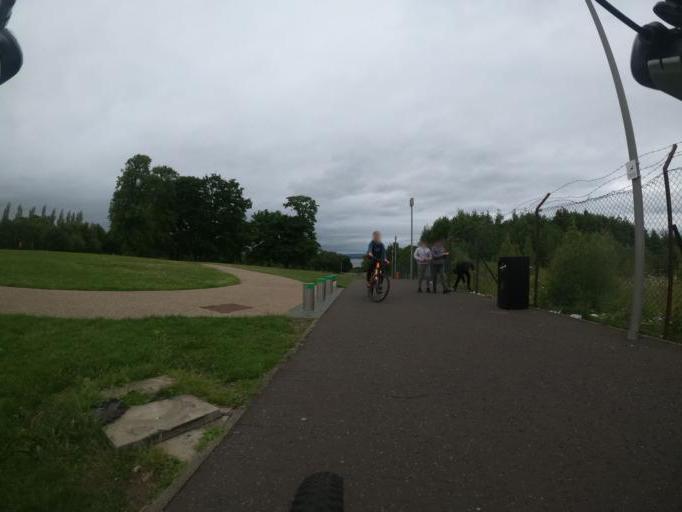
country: GB
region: Scotland
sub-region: Edinburgh
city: Edinburgh
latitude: 55.9792
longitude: -3.2508
